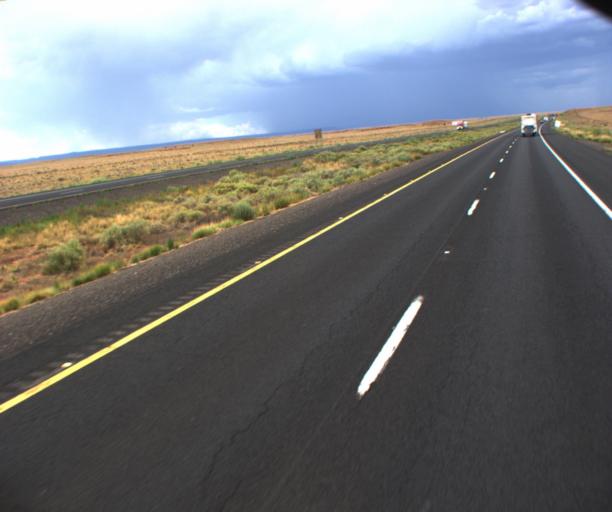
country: US
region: Arizona
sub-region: Coconino County
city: LeChee
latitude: 35.1145
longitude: -111.0691
